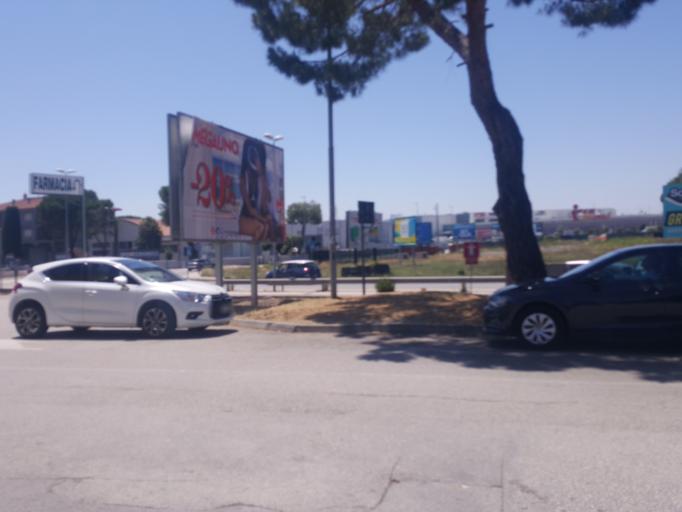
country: IT
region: The Marches
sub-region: Provincia di Macerata
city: Santa Maria Apparente
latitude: 43.2953
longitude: 13.7060
